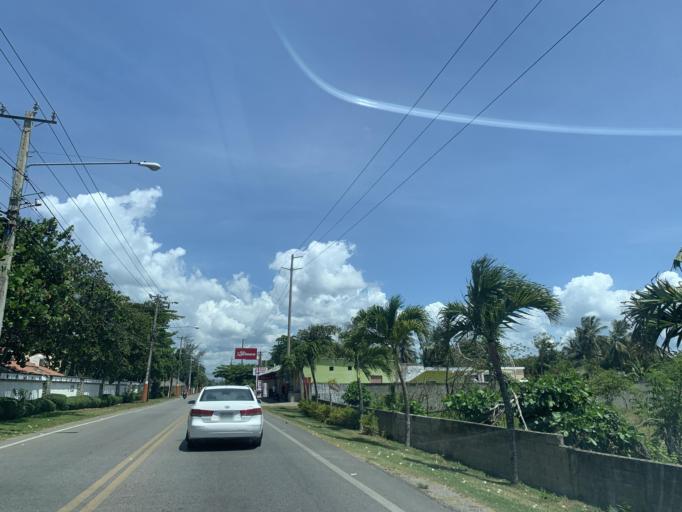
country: DO
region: Puerto Plata
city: Cabarete
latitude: 19.7443
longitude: -70.3944
